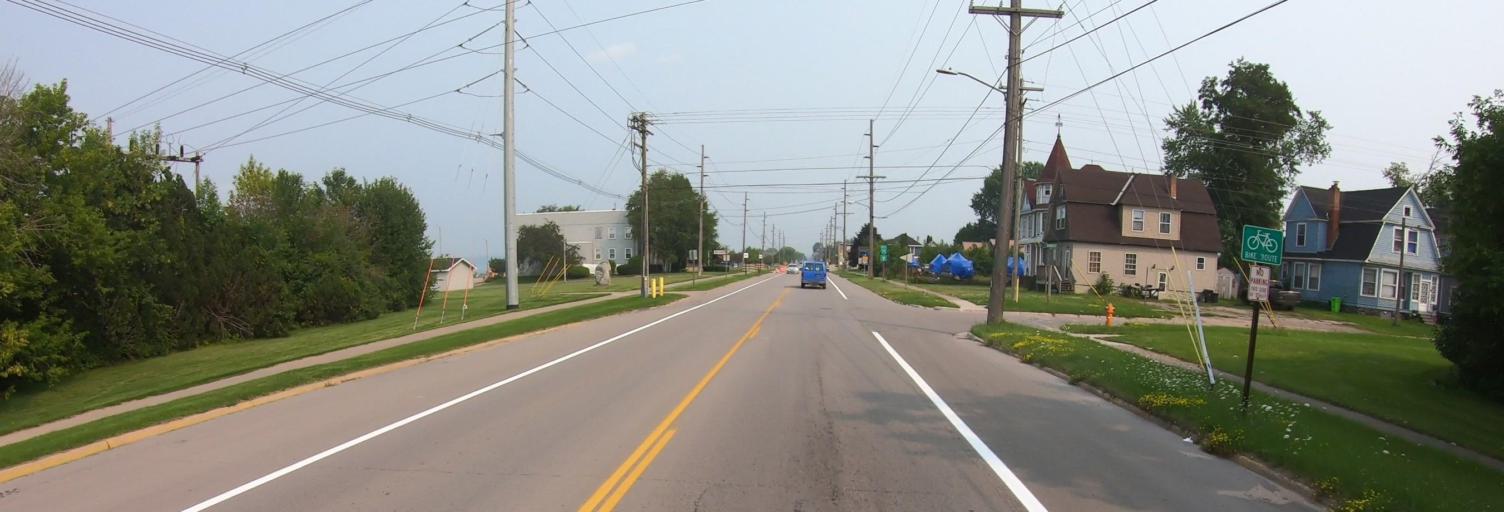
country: US
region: Michigan
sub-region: Chippewa County
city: Sault Ste. Marie
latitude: 46.4958
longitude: -84.3325
